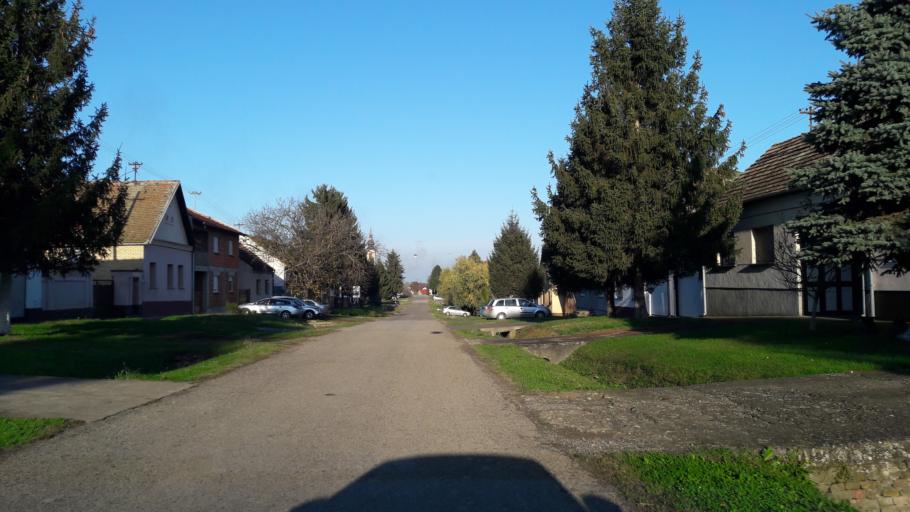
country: HR
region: Osjecko-Baranjska
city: Viskovci
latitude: 45.3410
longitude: 18.4536
